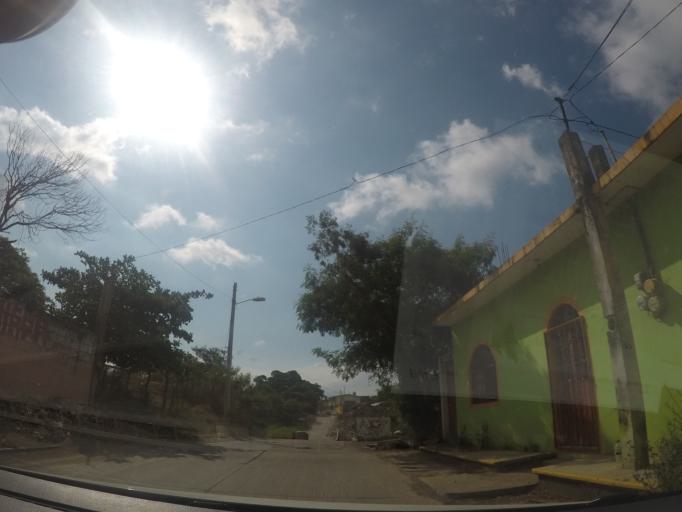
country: MX
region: Oaxaca
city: Juchitan de Zaragoza
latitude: 16.4288
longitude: -95.0274
